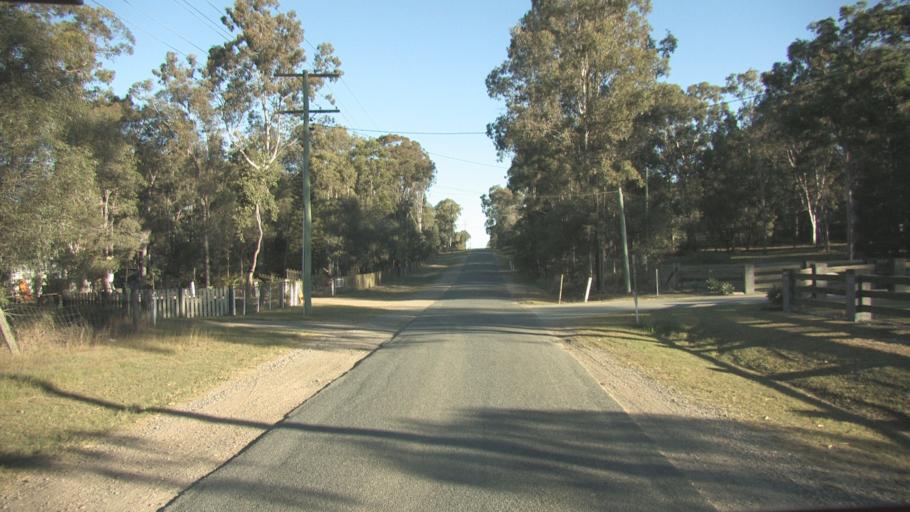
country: AU
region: Queensland
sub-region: Logan
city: Chambers Flat
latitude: -27.7711
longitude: 153.1297
